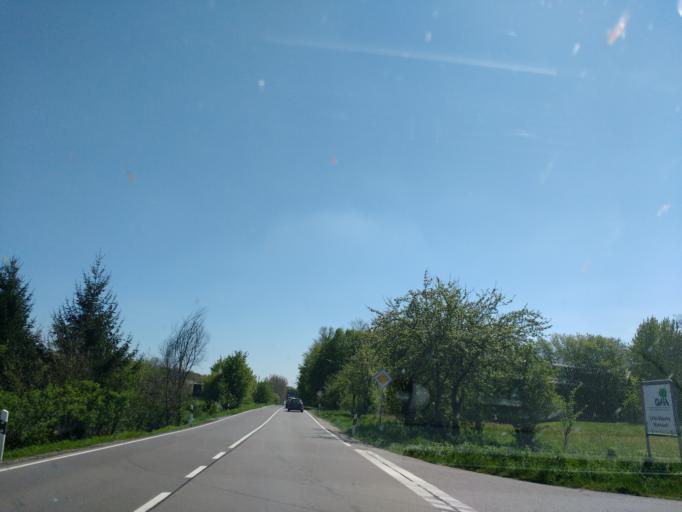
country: DE
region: Saxony-Anhalt
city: Deuben
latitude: 51.1217
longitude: 12.0697
